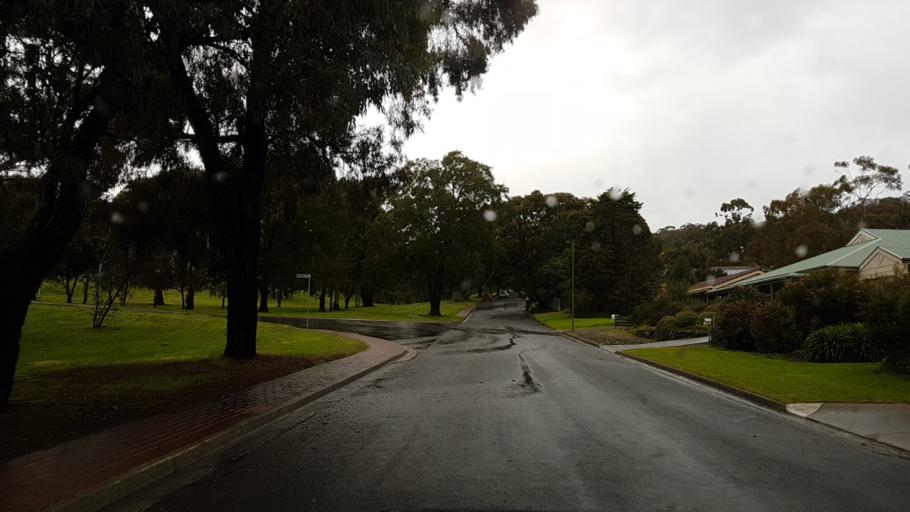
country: AU
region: South Australia
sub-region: Onkaparinga
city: Craigburn Farm
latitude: -35.0823
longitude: 138.5933
